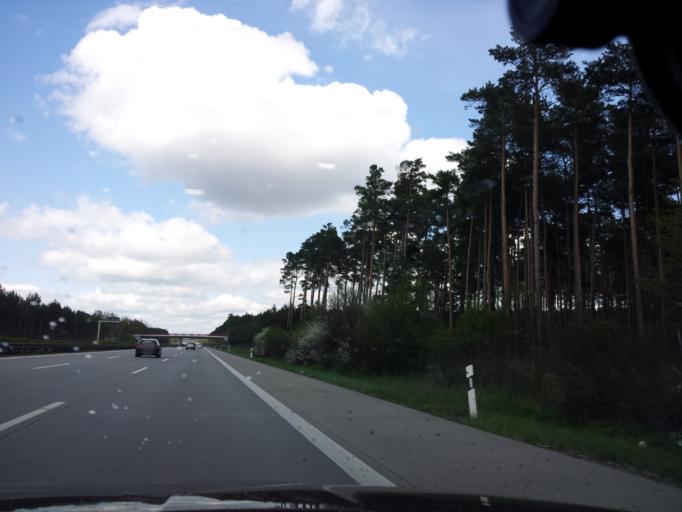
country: DE
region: Brandenburg
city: Grunheide
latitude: 52.3967
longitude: 13.7866
